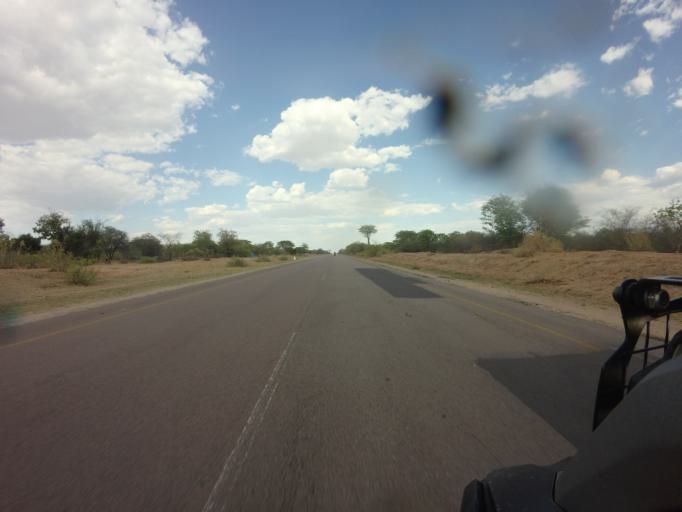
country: AO
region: Cunene
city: Ondjiva
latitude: -16.7362
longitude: 15.1441
